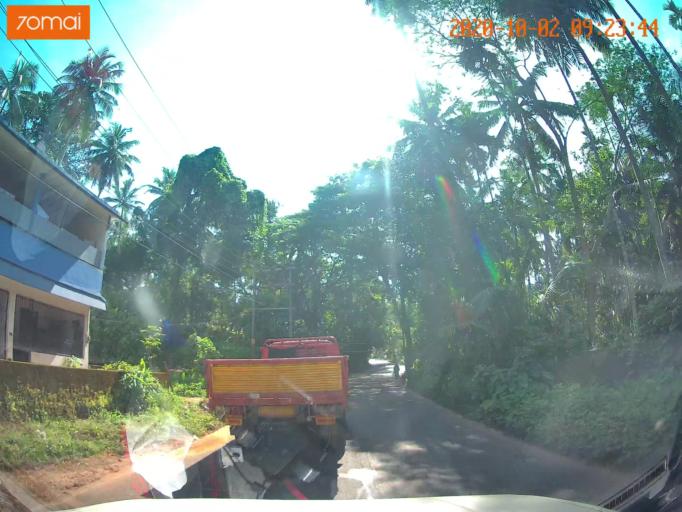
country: IN
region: Kerala
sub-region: Kozhikode
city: Naduvannur
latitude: 11.5836
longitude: 75.7600
